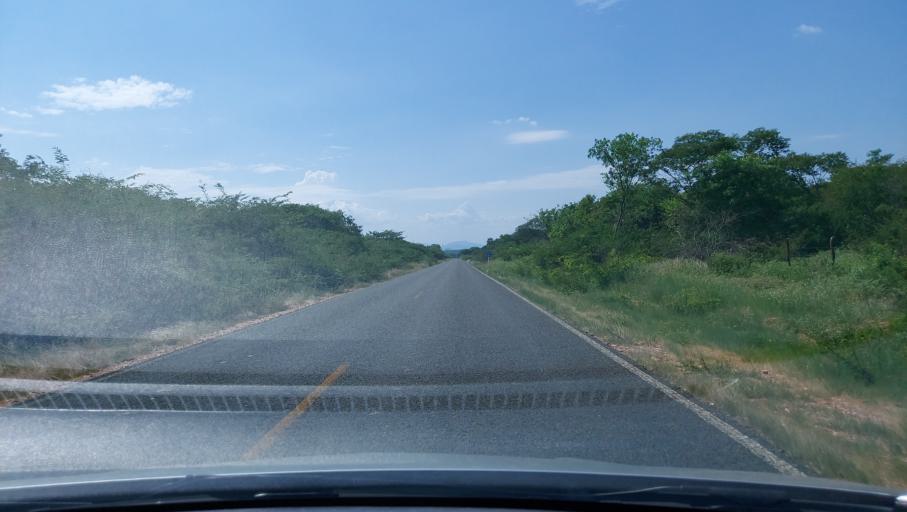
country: BR
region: Bahia
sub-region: Oliveira Dos Brejinhos
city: Beira Rio
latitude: -12.1815
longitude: -42.5416
